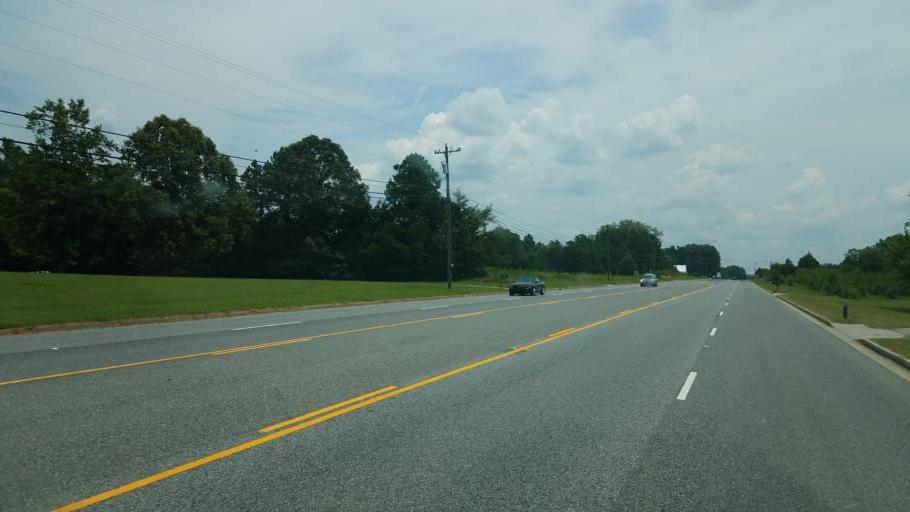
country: US
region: South Carolina
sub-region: York County
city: York
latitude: 35.0292
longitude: -81.2906
